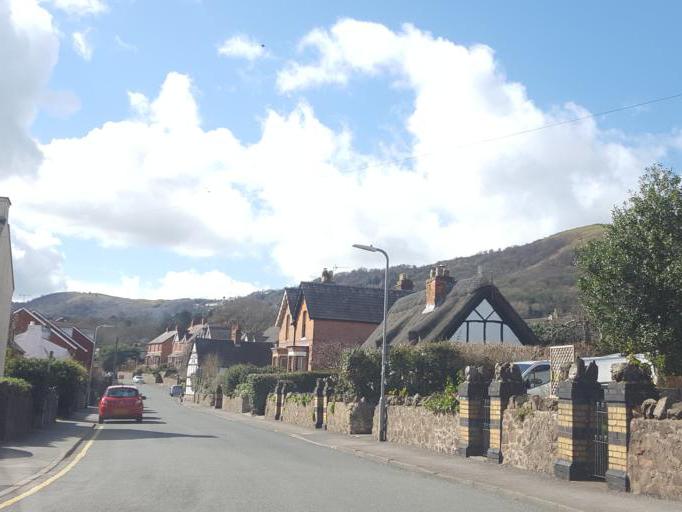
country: GB
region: England
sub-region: Worcestershire
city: Great Malvern
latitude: 52.1070
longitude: -2.3167
